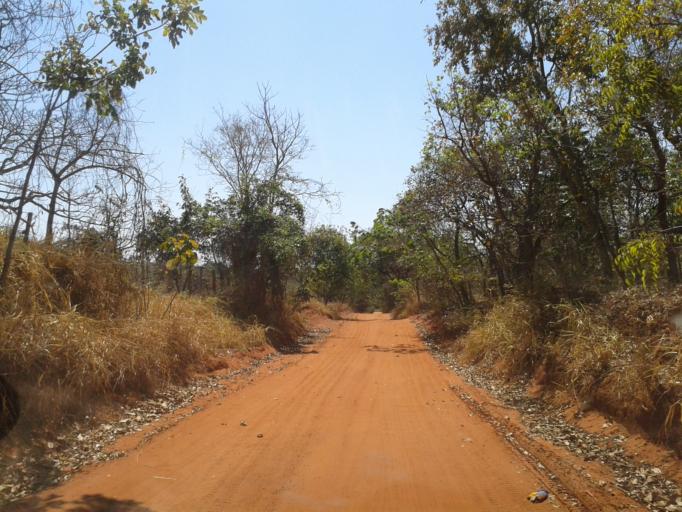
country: BR
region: Minas Gerais
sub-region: Ituiutaba
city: Ituiutaba
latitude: -19.0898
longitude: -49.2979
